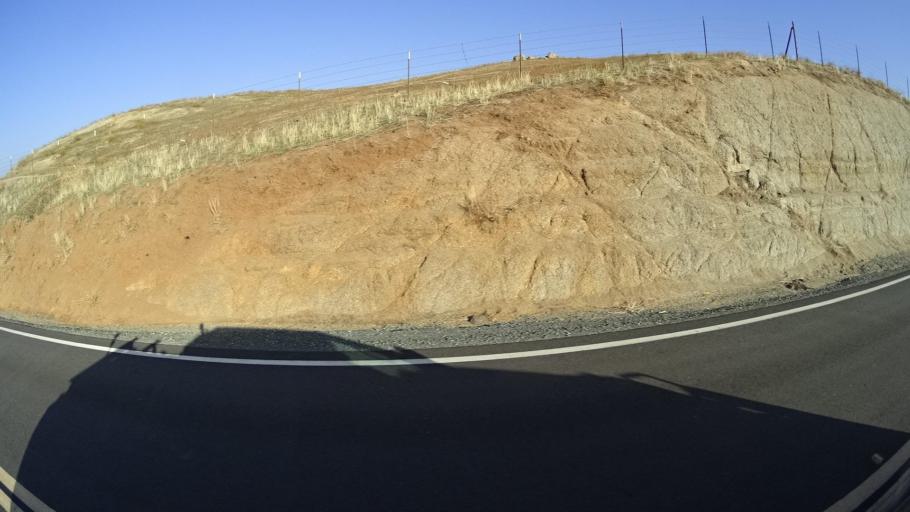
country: US
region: California
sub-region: Tulare County
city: Richgrove
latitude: 35.7422
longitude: -118.9053
